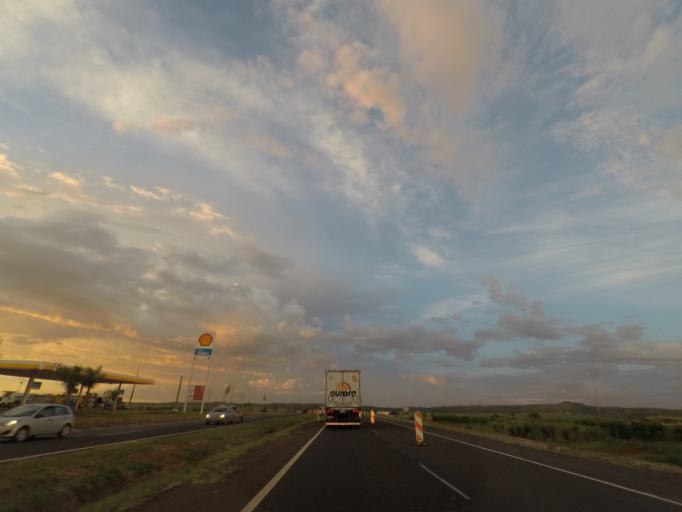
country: BR
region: Minas Gerais
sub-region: Uberaba
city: Uberaba
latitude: -19.6278
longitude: -48.0146
